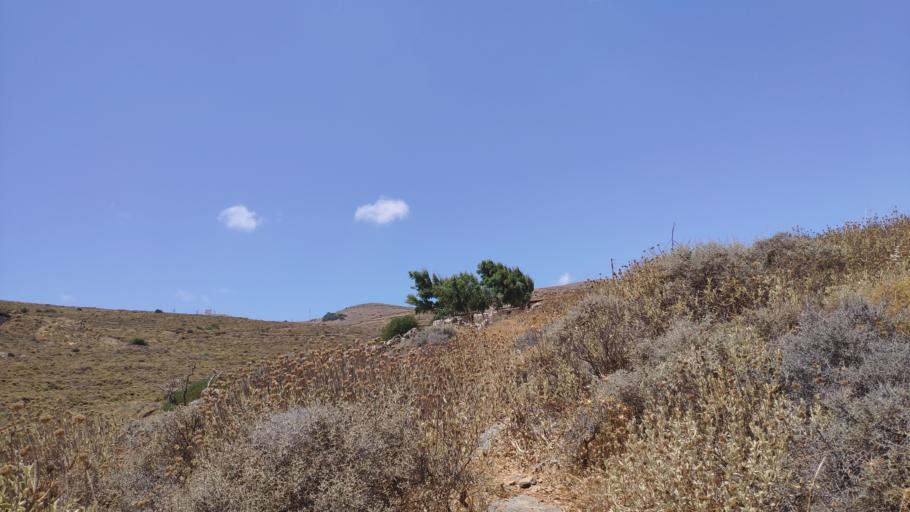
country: GR
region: South Aegean
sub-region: Nomos Kykladon
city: Kythnos
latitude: 37.3802
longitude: 24.4541
